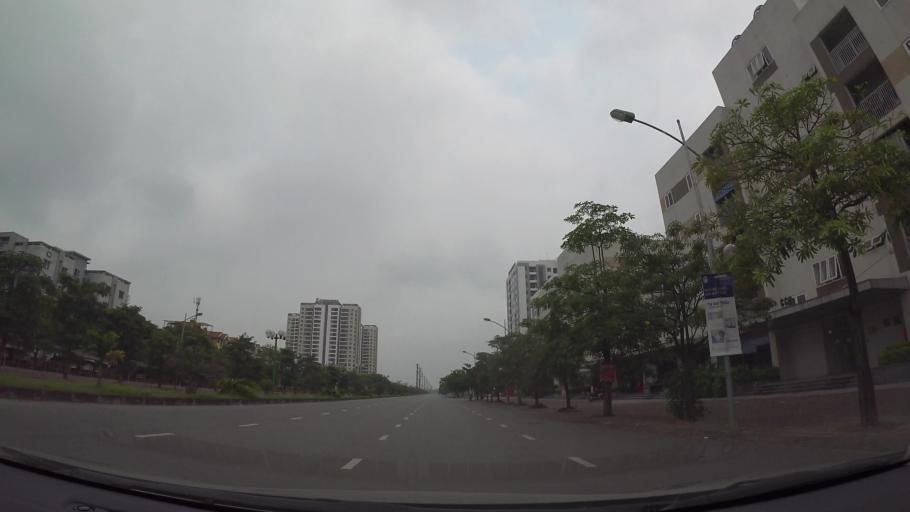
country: VN
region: Ha Noi
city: Trau Quy
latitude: 21.0612
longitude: 105.9132
